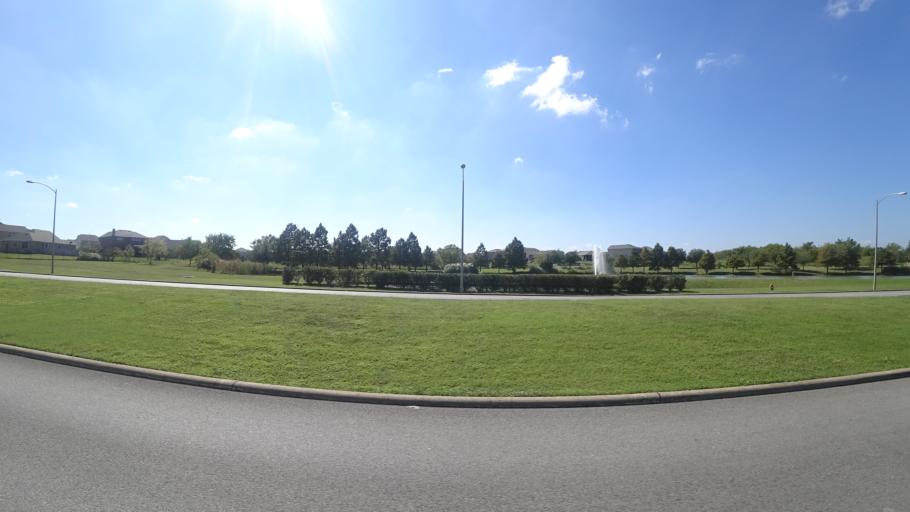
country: US
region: Texas
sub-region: Travis County
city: Manor
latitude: 30.3493
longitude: -97.6142
